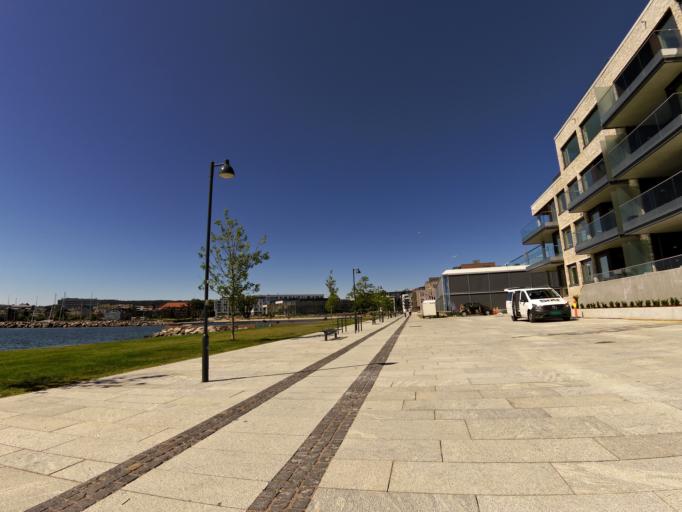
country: NO
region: Vest-Agder
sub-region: Kristiansand
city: Kristiansand
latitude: 58.1442
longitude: 8.0097
